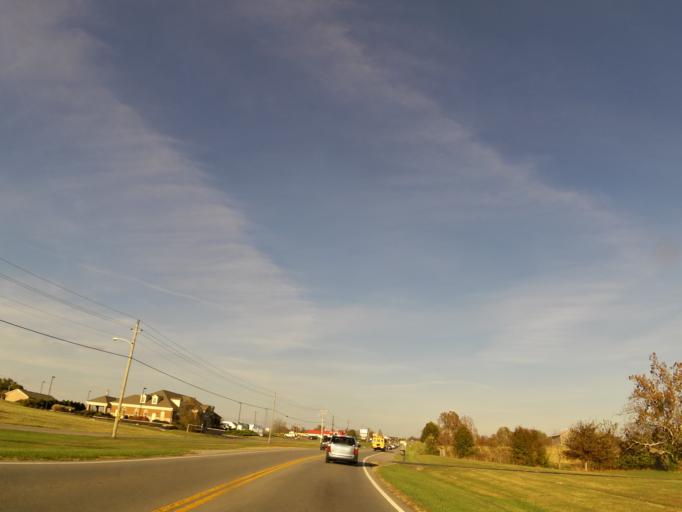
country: US
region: Kentucky
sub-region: Garrard County
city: Lancaster
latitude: 37.5991
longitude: -84.5934
